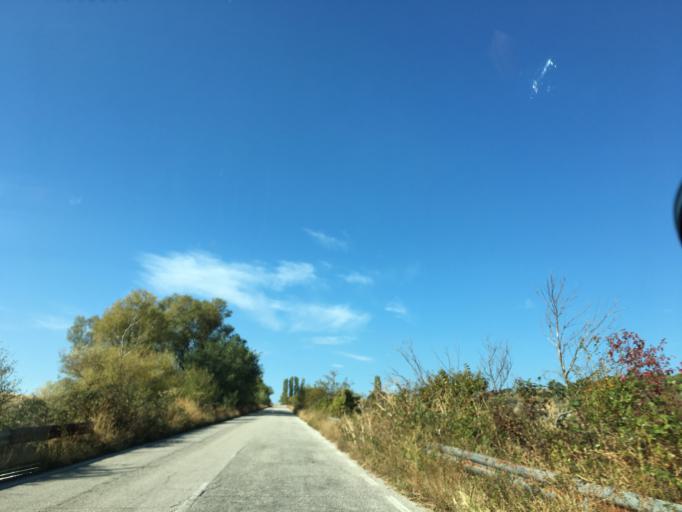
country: BG
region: Khaskovo
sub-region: Obshtina Ivaylovgrad
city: Ivaylovgrad
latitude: 41.5157
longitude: 26.0064
